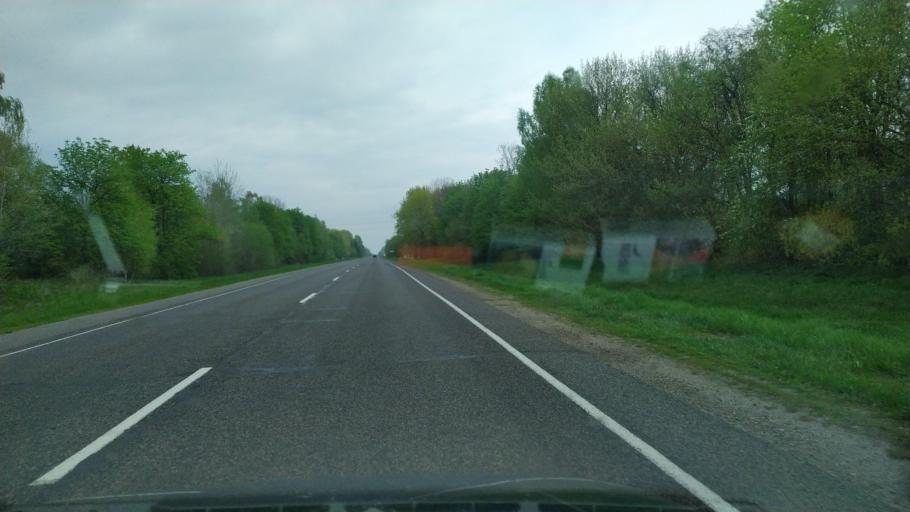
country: BY
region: Brest
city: Horad Kobryn
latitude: 52.2833
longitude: 24.4859
